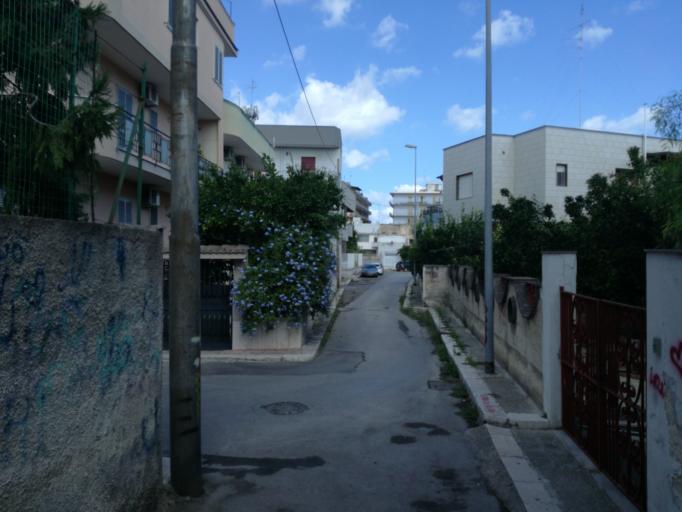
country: IT
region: Apulia
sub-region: Provincia di Bari
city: Triggiano
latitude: 41.0646
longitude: 16.9291
